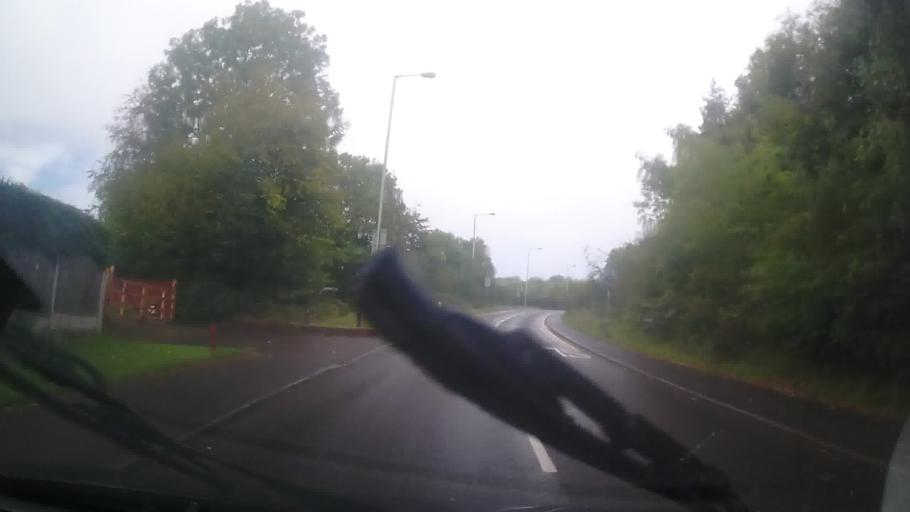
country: GB
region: England
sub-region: Shropshire
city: Much Wenlock
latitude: 52.6043
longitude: -2.5570
